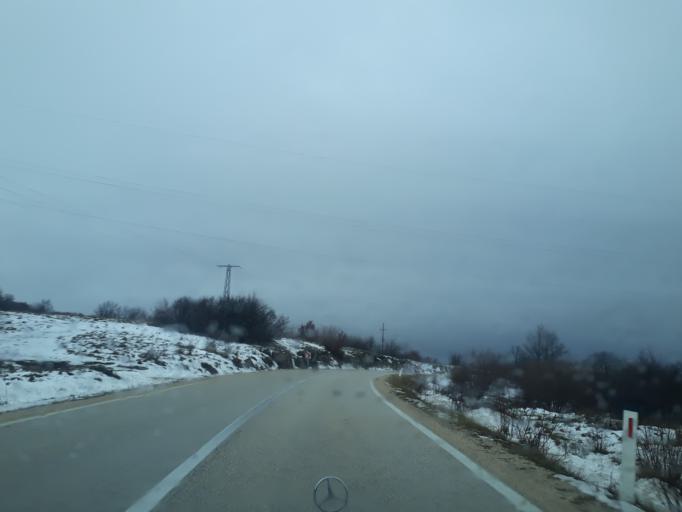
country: BA
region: Federation of Bosnia and Herzegovina
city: Tomislavgrad
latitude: 43.7877
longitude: 17.2225
